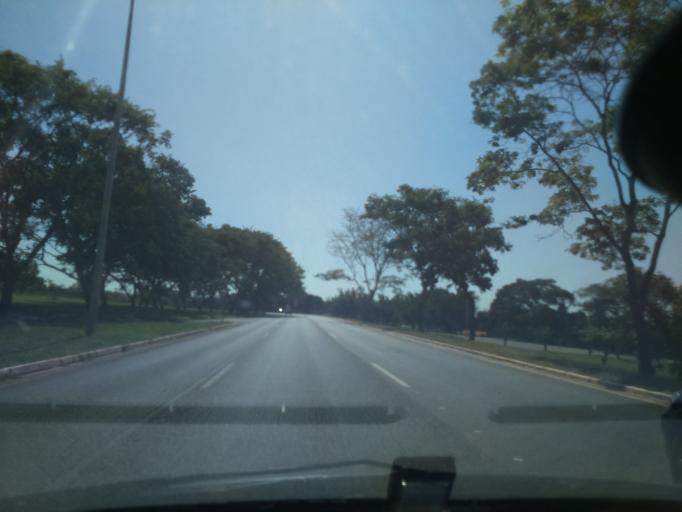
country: BR
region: Federal District
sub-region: Brasilia
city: Brasilia
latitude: -15.8329
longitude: -47.8935
